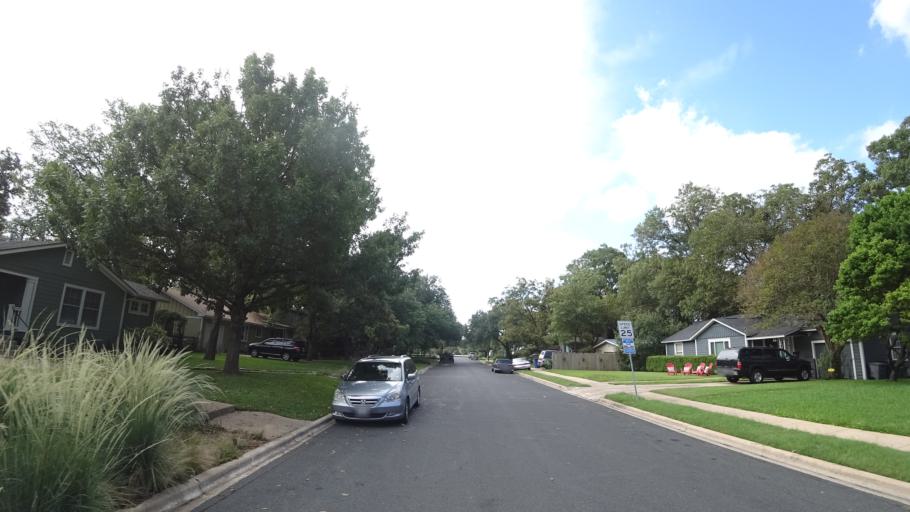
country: US
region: Texas
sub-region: Travis County
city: Austin
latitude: 30.3373
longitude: -97.7433
